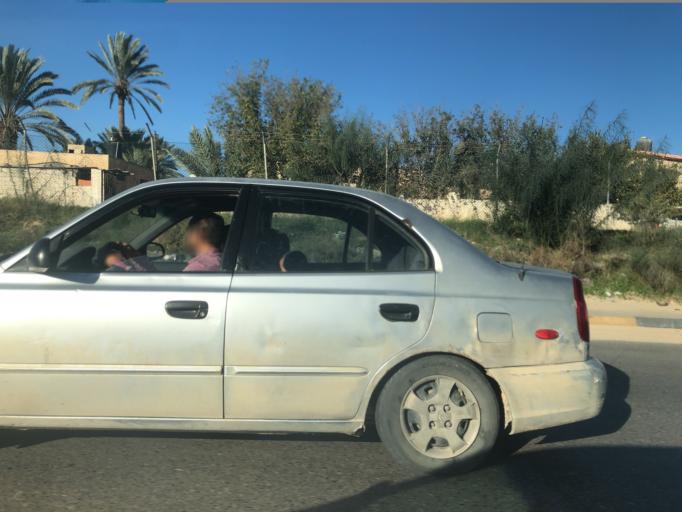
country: LY
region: Tripoli
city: Tagiura
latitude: 32.8694
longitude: 13.2734
